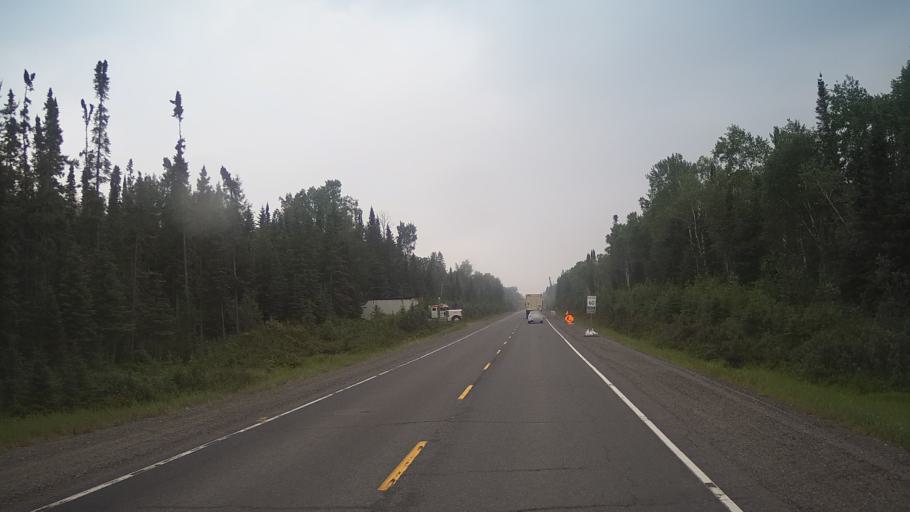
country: CA
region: Ontario
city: Greenstone
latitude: 49.1885
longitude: -88.2186
